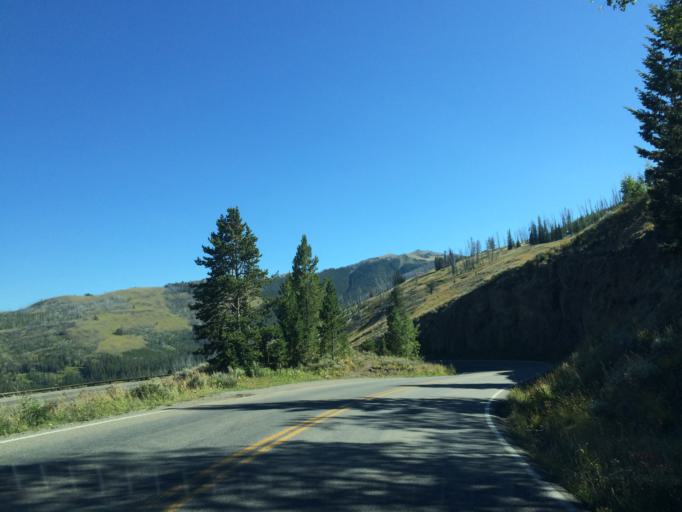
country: US
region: Montana
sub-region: Gallatin County
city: West Yellowstone
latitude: 44.8393
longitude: -110.4375
